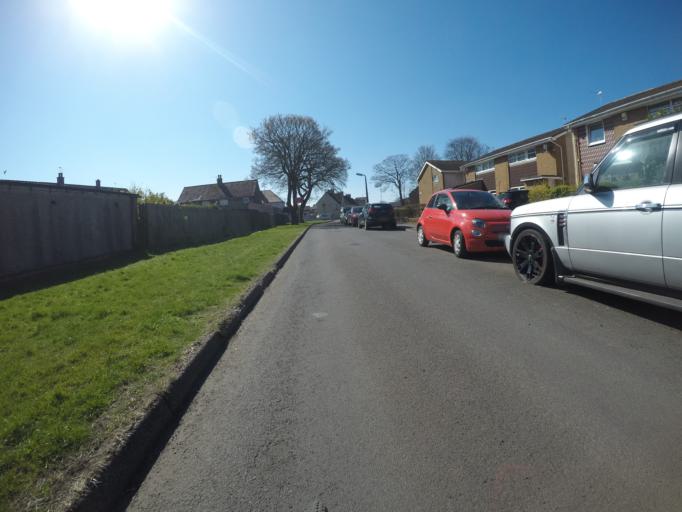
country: GB
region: Scotland
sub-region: North Ayrshire
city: Irvine
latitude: 55.6274
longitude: -4.6716
